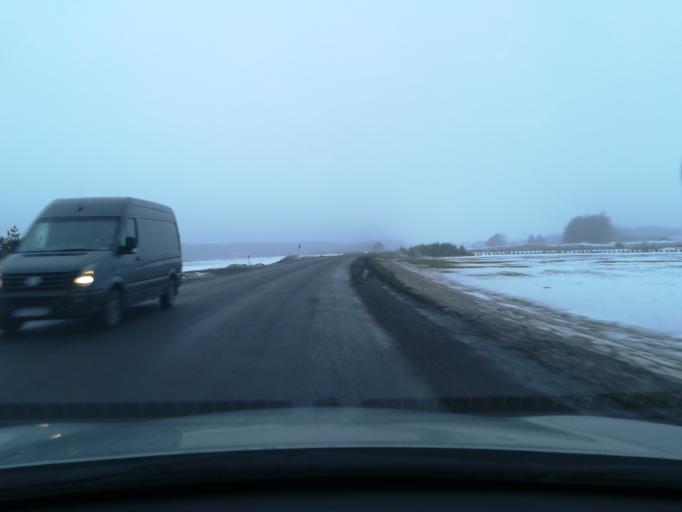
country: EE
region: Harju
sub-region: Raasiku vald
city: Arukula
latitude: 59.3503
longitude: 25.0869
